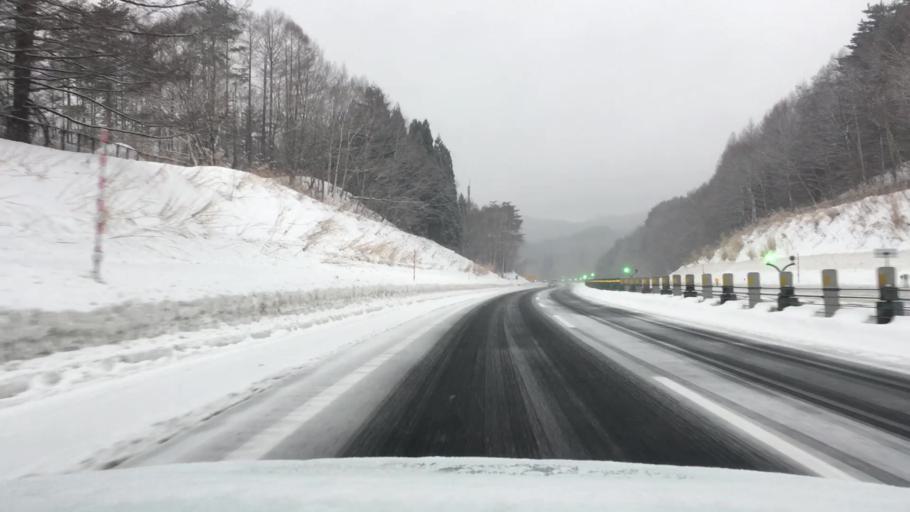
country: JP
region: Akita
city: Hanawa
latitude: 40.1185
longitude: 141.0157
